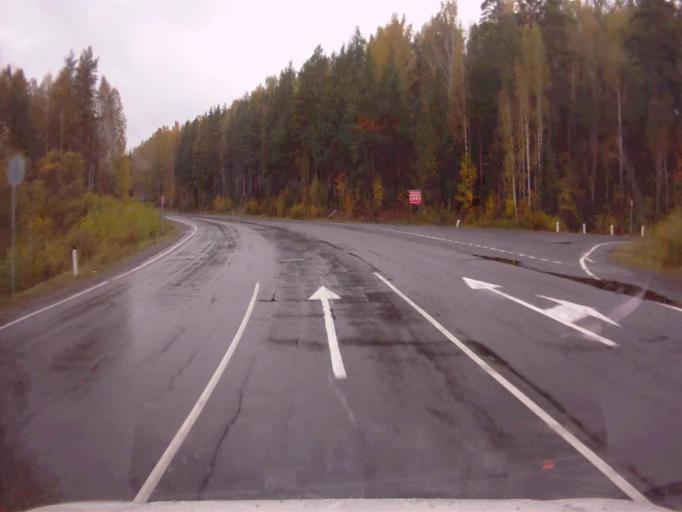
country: RU
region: Chelyabinsk
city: Verkhniy Ufaley
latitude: 55.9661
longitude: 60.3818
